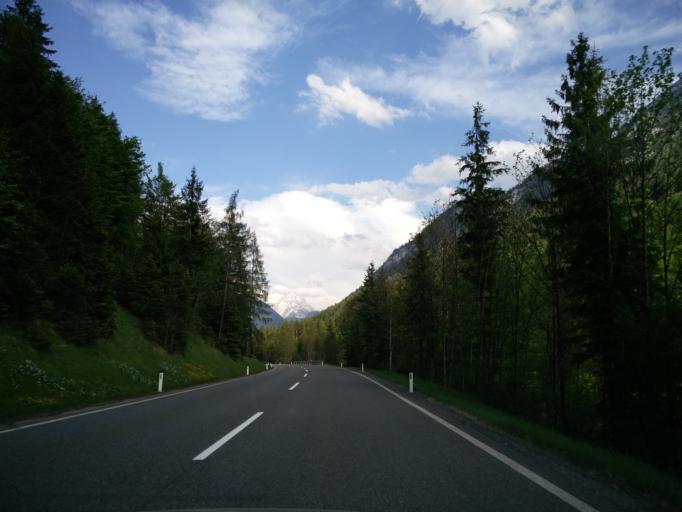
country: AT
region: Salzburg
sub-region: Politischer Bezirk Zell am See
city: Lofer
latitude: 47.5827
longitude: 12.6360
